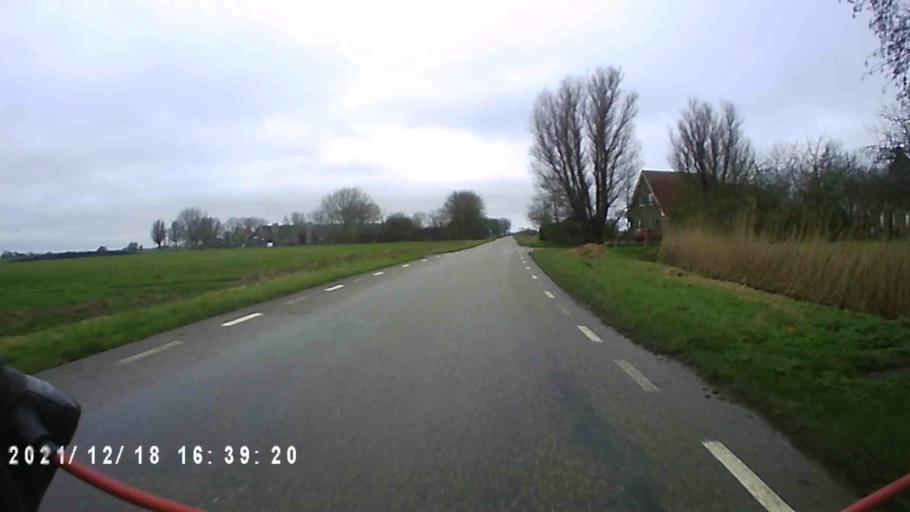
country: NL
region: Friesland
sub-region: Gemeente Dongeradeel
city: Dokkum
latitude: 53.3599
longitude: 6.0071
